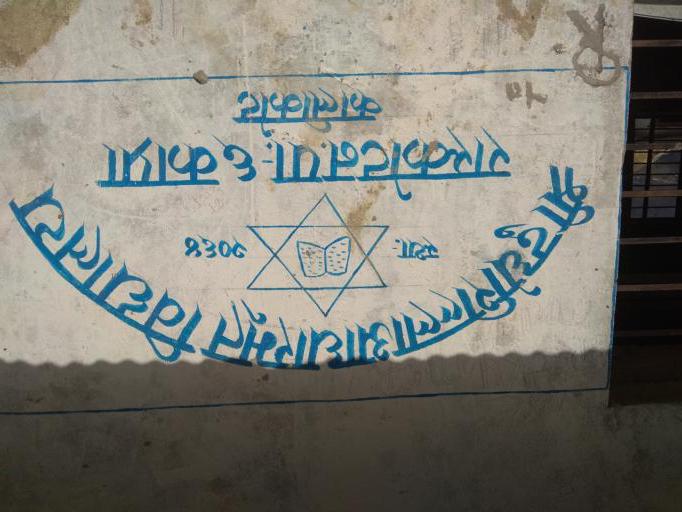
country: NP
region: Far Western
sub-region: Seti Zone
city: Achham
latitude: 29.2448
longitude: 81.6232
